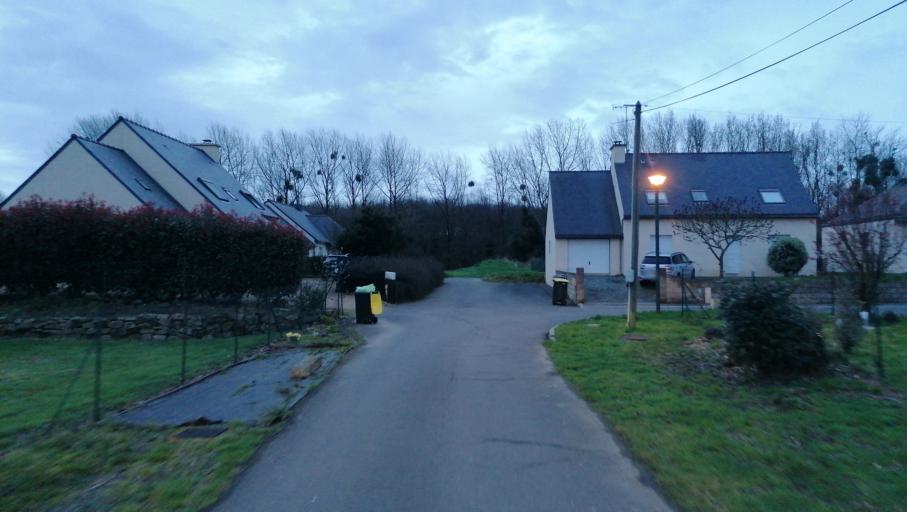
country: FR
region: Brittany
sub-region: Departement des Cotes-d'Armor
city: Saint-Agathon
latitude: 48.5784
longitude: -3.0645
